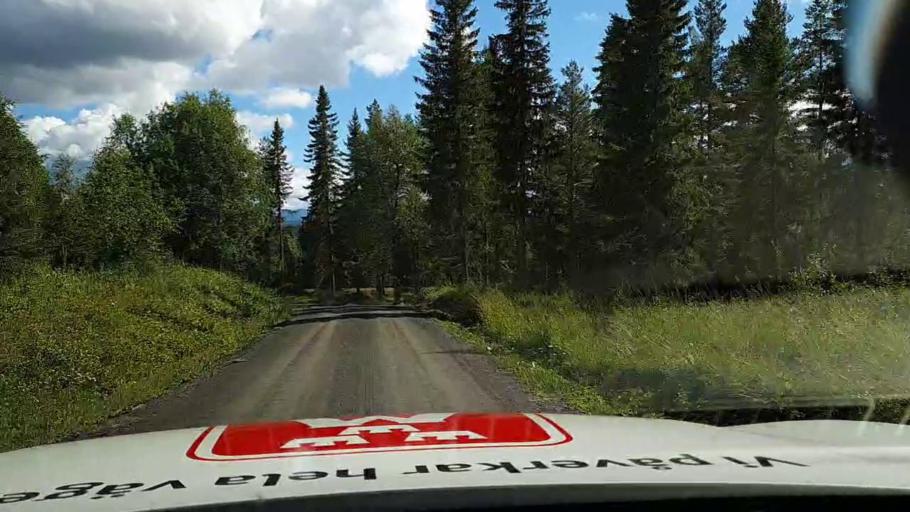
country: SE
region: Jaemtland
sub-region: Krokoms Kommun
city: Valla
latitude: 63.3286
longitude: 13.7348
